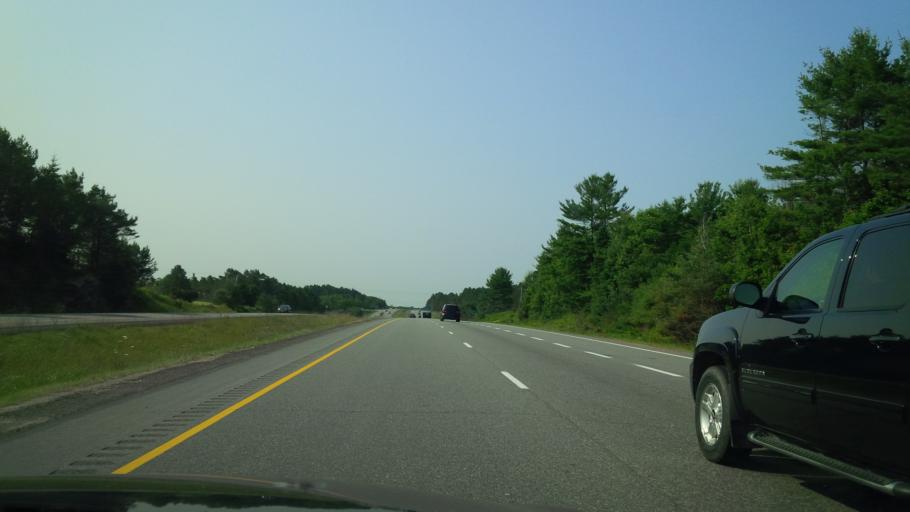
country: CA
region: Ontario
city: Bracebridge
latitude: 45.0795
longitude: -79.2968
